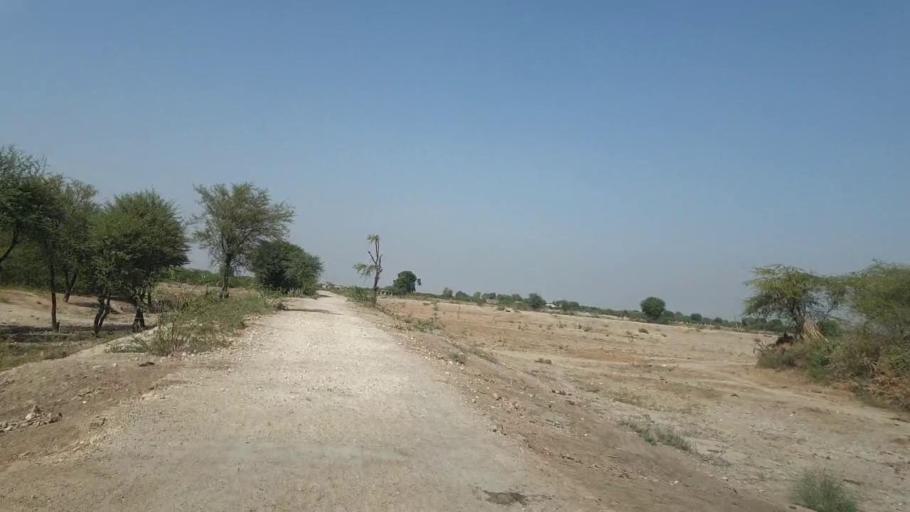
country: PK
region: Sindh
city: Nabisar
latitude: 24.9988
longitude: 69.5292
